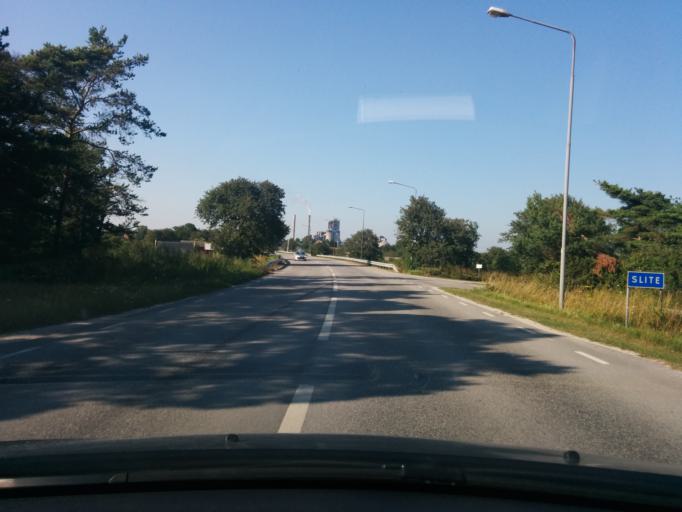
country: SE
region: Gotland
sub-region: Gotland
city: Slite
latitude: 57.6933
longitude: 18.7984
